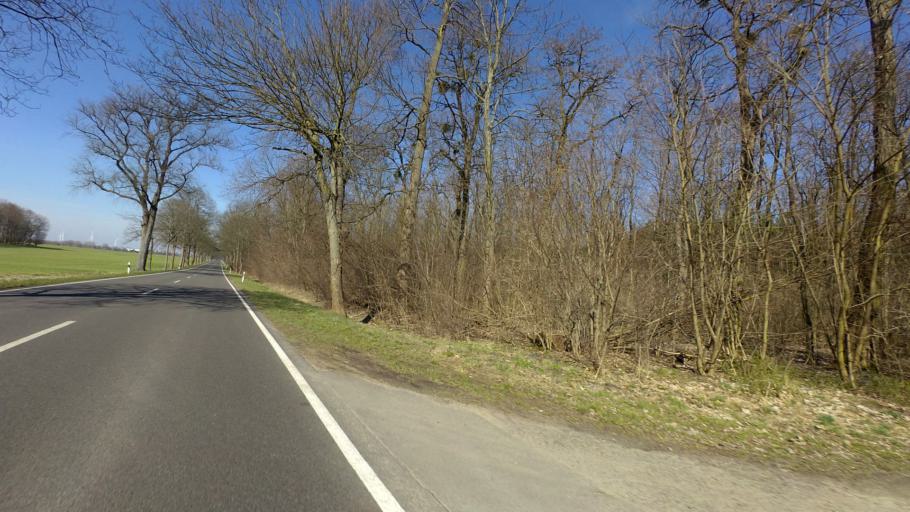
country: DE
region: Brandenburg
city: Werftpfuhl
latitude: 52.7218
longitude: 13.8375
